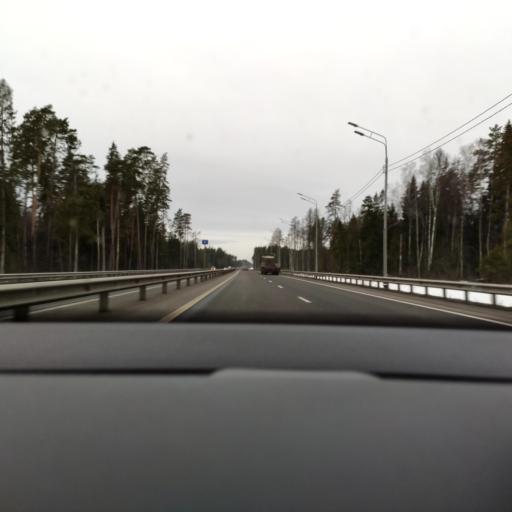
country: RU
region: Moskovskaya
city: Bol'shiye Vyazemy
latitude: 55.6600
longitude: 36.9600
